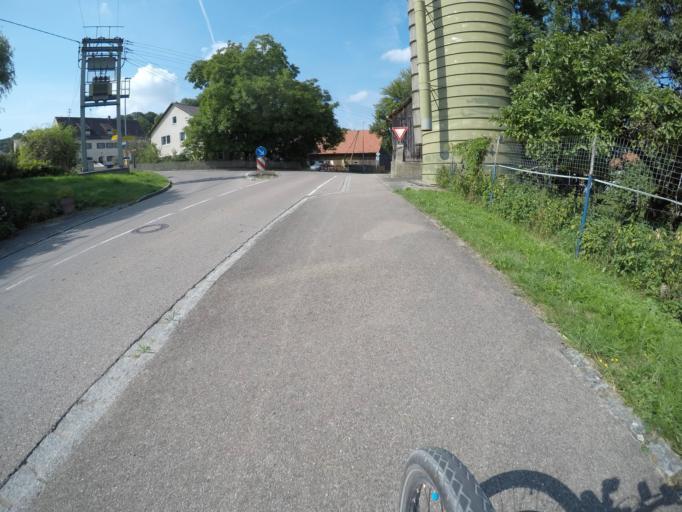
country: DE
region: Bavaria
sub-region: Swabia
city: Nordendorf
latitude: 48.5830
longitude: 10.8247
